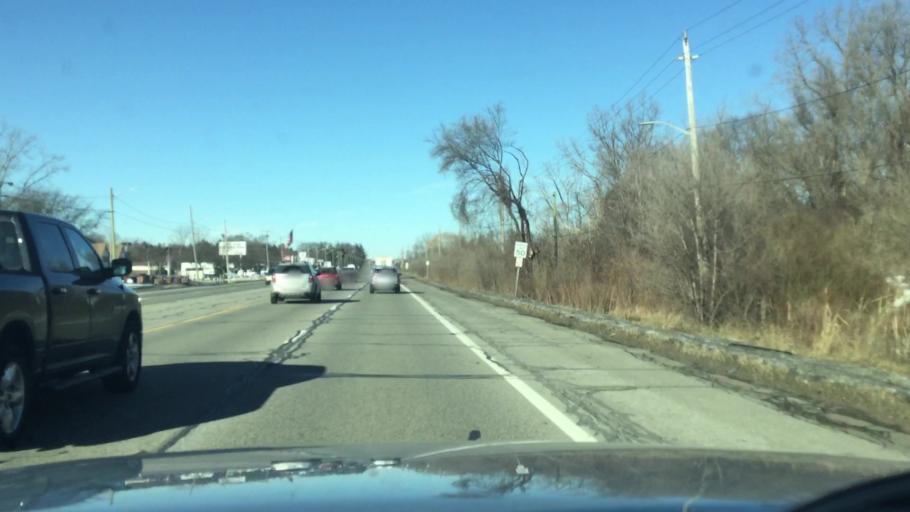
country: US
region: Michigan
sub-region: Oakland County
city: Keego Harbor
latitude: 42.6445
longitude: -83.3592
